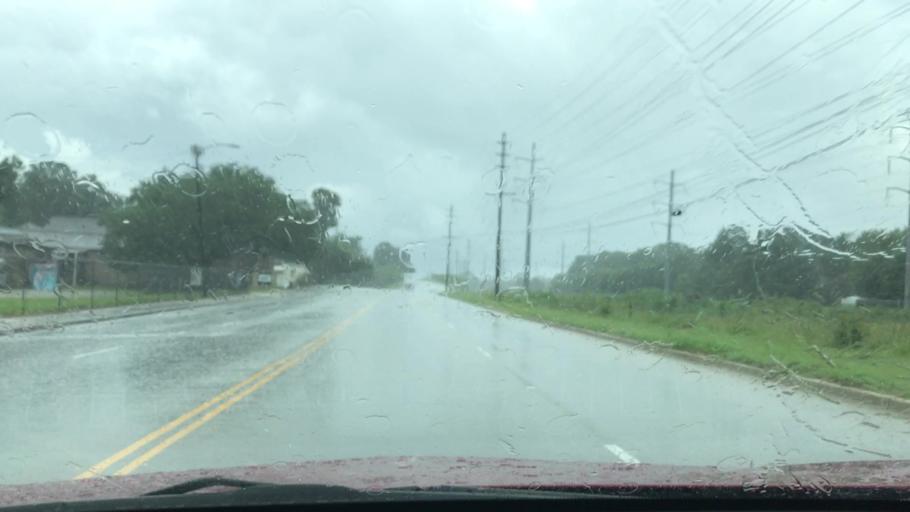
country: US
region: South Carolina
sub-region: Charleston County
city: North Charleston
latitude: 32.8474
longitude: -79.9822
